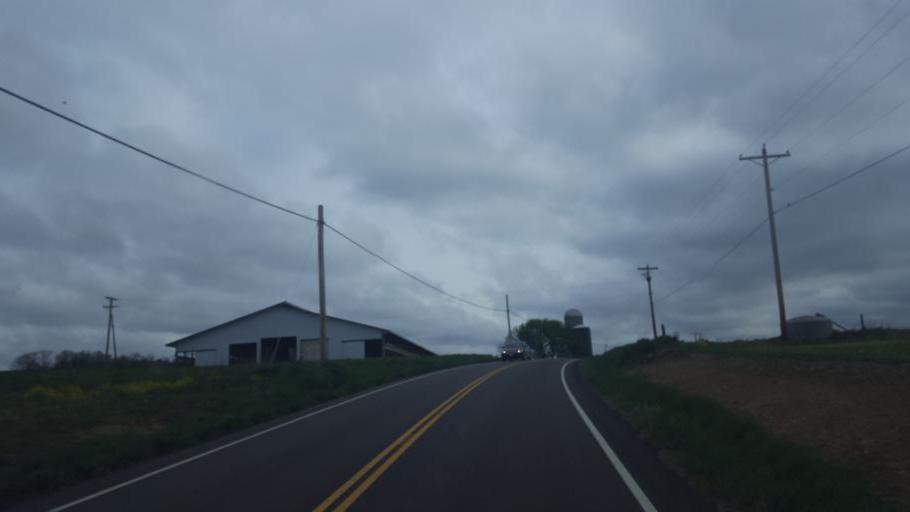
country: US
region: Ohio
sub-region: Knox County
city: Danville
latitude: 40.4652
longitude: -82.2492
